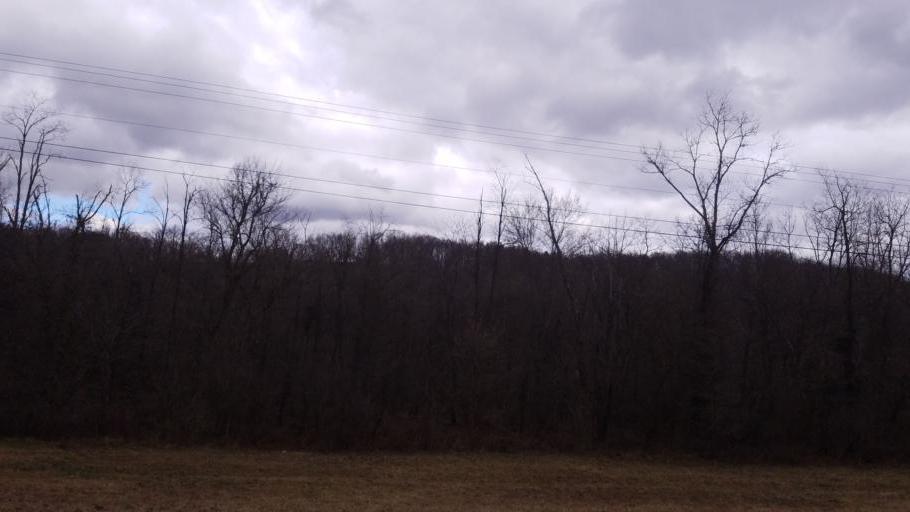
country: US
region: Ohio
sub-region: Muskingum County
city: Frazeysburg
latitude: 40.0590
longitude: -82.1459
